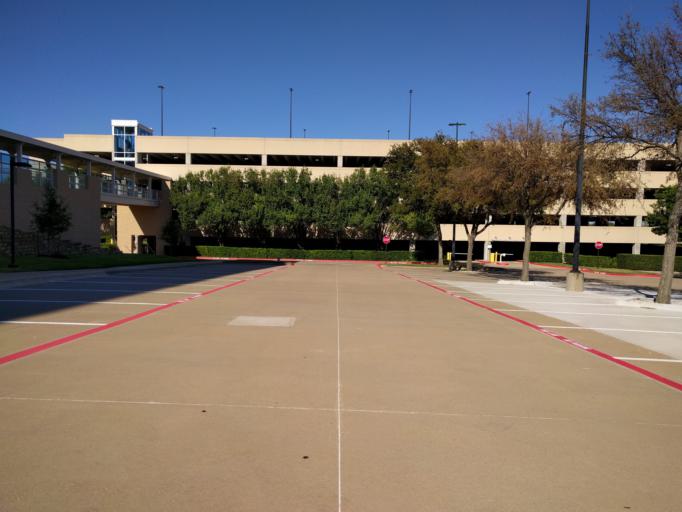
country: US
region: Texas
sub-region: Collin County
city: Plano
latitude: 32.9855
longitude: -96.7057
